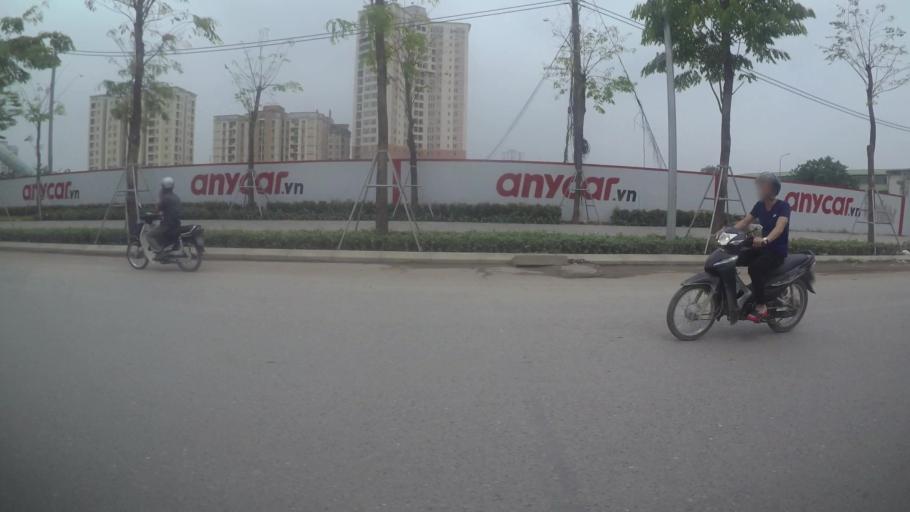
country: VN
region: Ha Noi
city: Tay Ho
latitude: 21.0680
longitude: 105.7850
